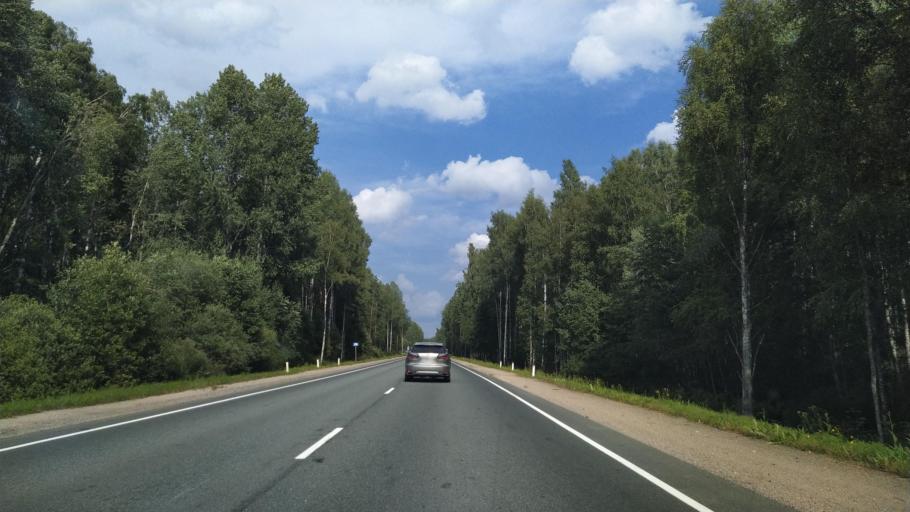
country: RU
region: Pskov
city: Porkhov
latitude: 57.8670
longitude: 29.6049
